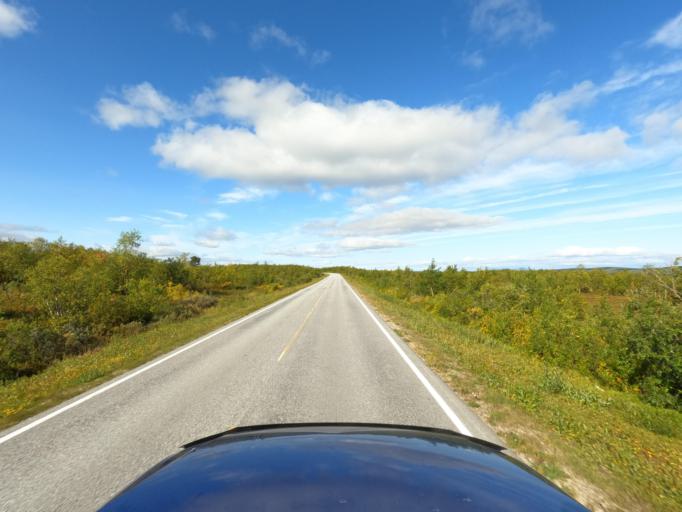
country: NO
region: Finnmark Fylke
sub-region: Karasjok
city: Karasjohka
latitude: 69.6059
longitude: 25.3235
